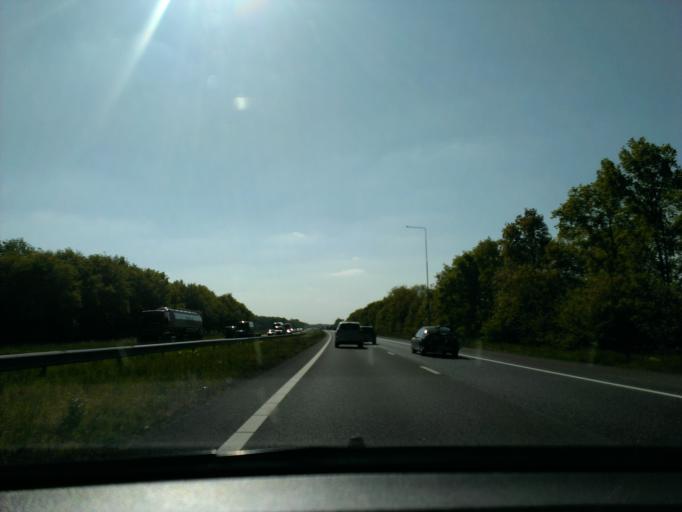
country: NL
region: Gelderland
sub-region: Gemeente Lochem
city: Harfsen
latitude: 52.2427
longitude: 6.2760
